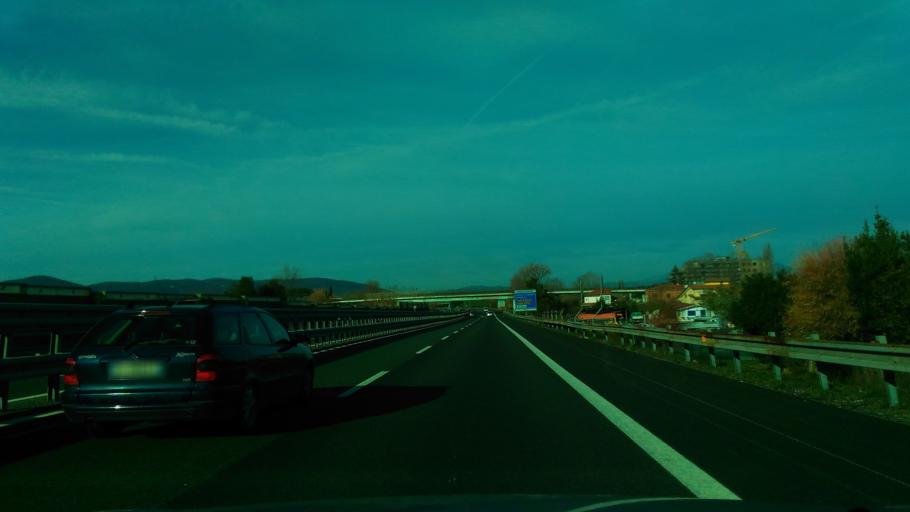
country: IT
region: Tuscany
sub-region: Provincia di Massa-Carrara
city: Marina di Carrara
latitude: 44.0496
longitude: 10.0402
